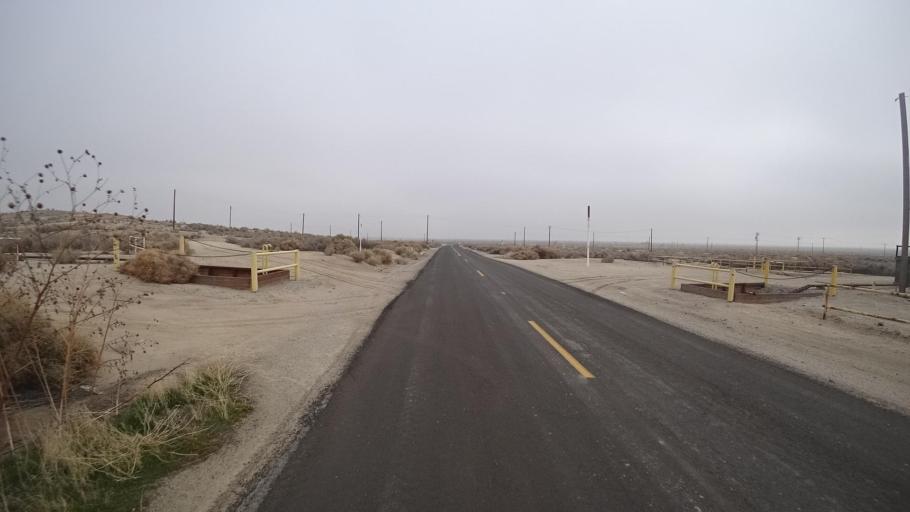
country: US
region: California
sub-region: Kern County
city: Maricopa
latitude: 35.0755
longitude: -119.3608
